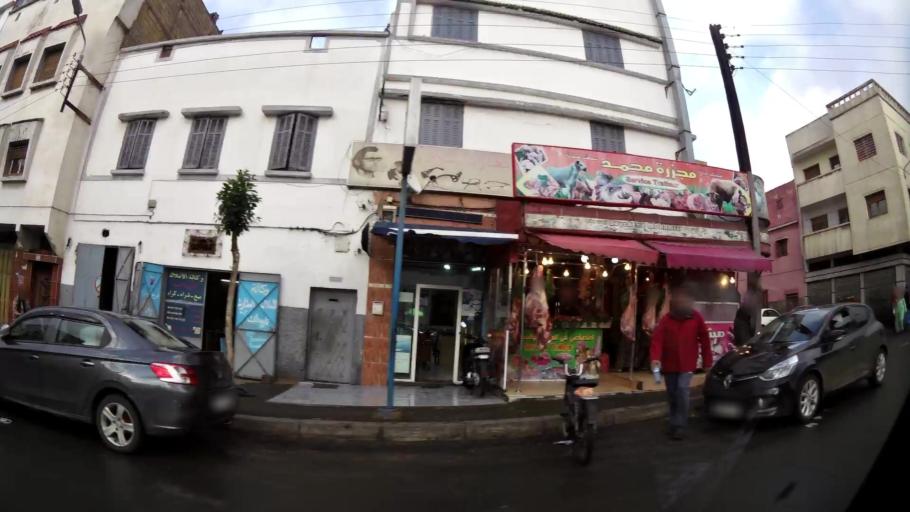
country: MA
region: Grand Casablanca
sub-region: Casablanca
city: Casablanca
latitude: 33.5508
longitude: -7.5740
